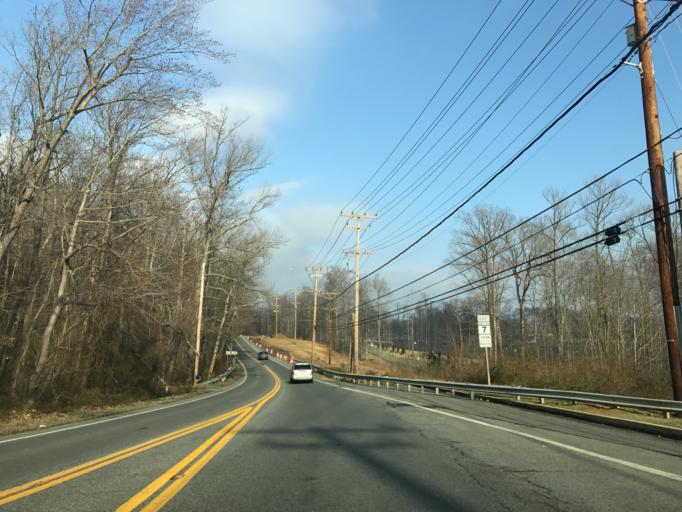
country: US
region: Maryland
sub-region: Harford County
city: Riverside
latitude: 39.4873
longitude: -76.2319
